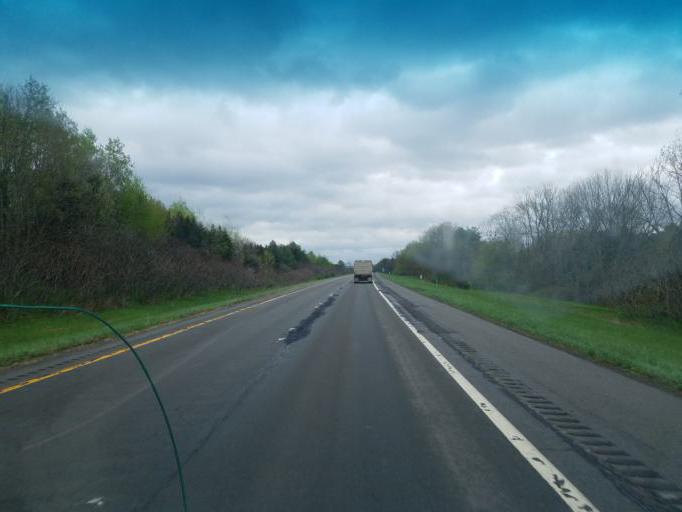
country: US
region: New York
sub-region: Chautauqua County
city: Falconer
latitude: 42.1371
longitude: -79.1610
